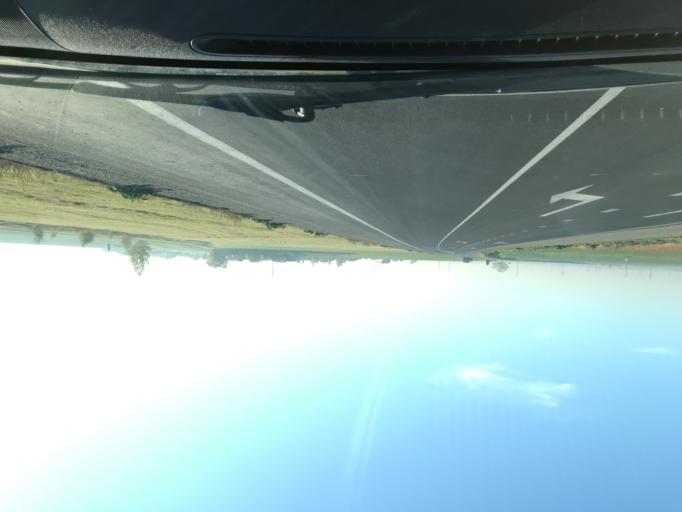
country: BY
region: Brest
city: Asnyezhytsy
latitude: 52.1892
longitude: 26.0964
